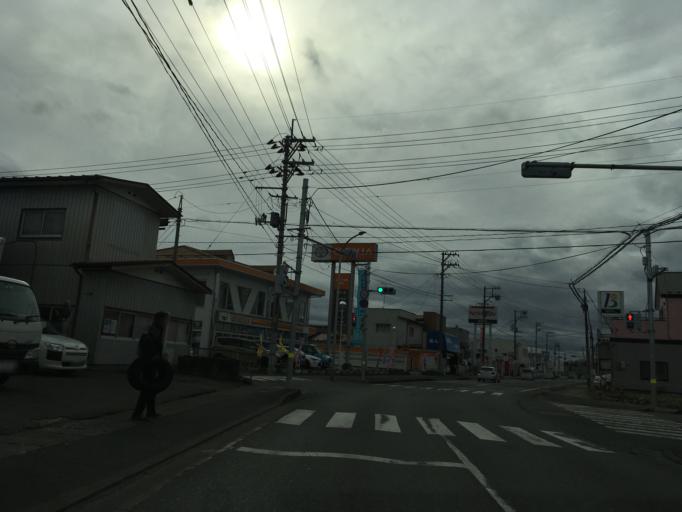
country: JP
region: Miyagi
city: Wakuya
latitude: 38.6892
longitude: 141.2051
